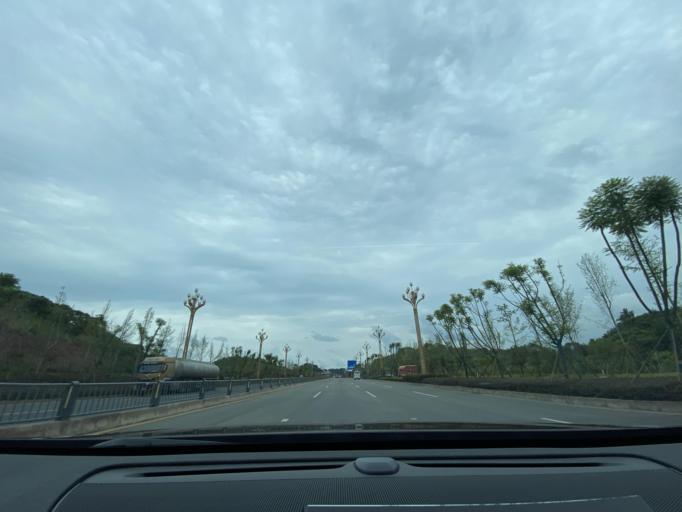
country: CN
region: Sichuan
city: Jiancheng
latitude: 30.4781
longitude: 104.4877
